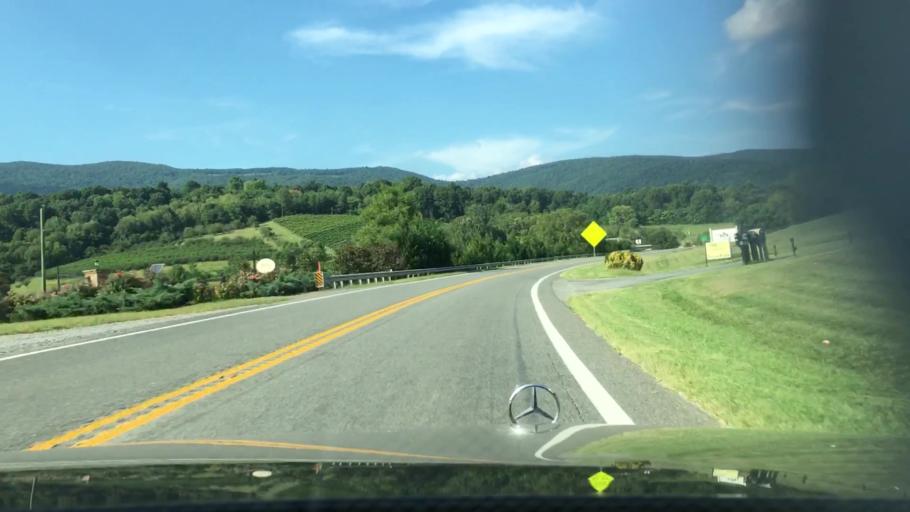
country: US
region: Virginia
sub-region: City of Waynesboro
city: Waynesboro
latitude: 38.0179
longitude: -78.8226
